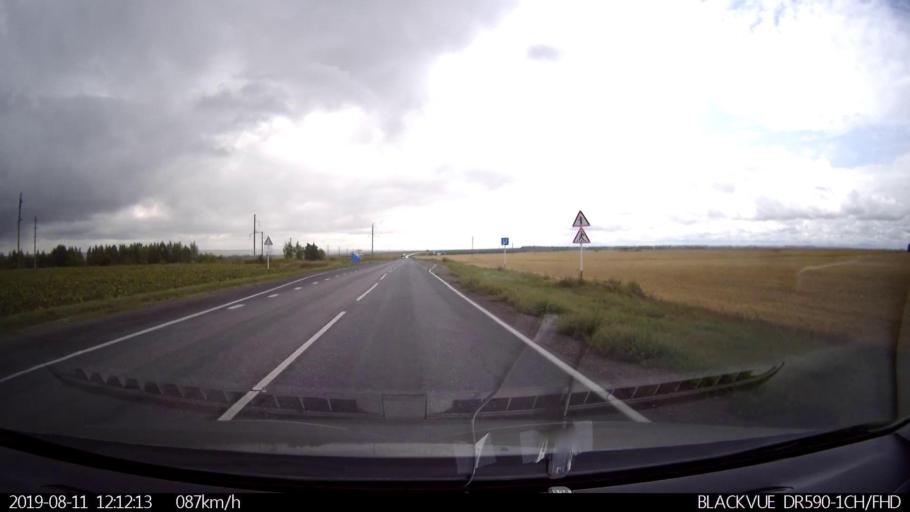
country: RU
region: Ulyanovsk
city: Silikatnyy
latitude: 53.9760
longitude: 47.9977
